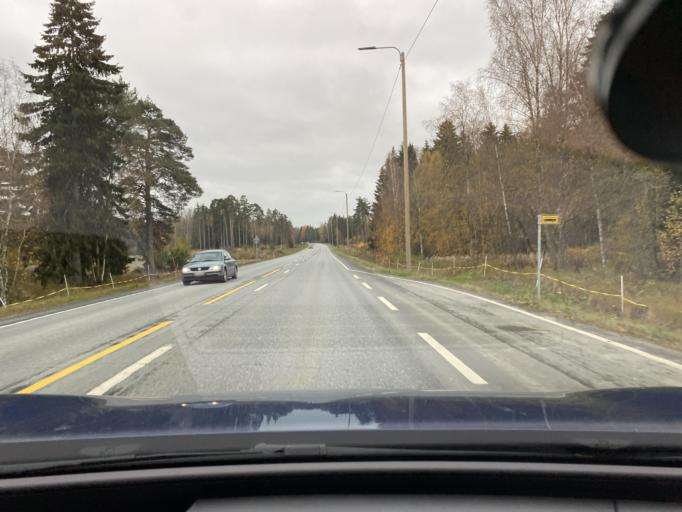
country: FI
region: Varsinais-Suomi
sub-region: Vakka-Suomi
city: Laitila
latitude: 60.9402
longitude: 21.6025
